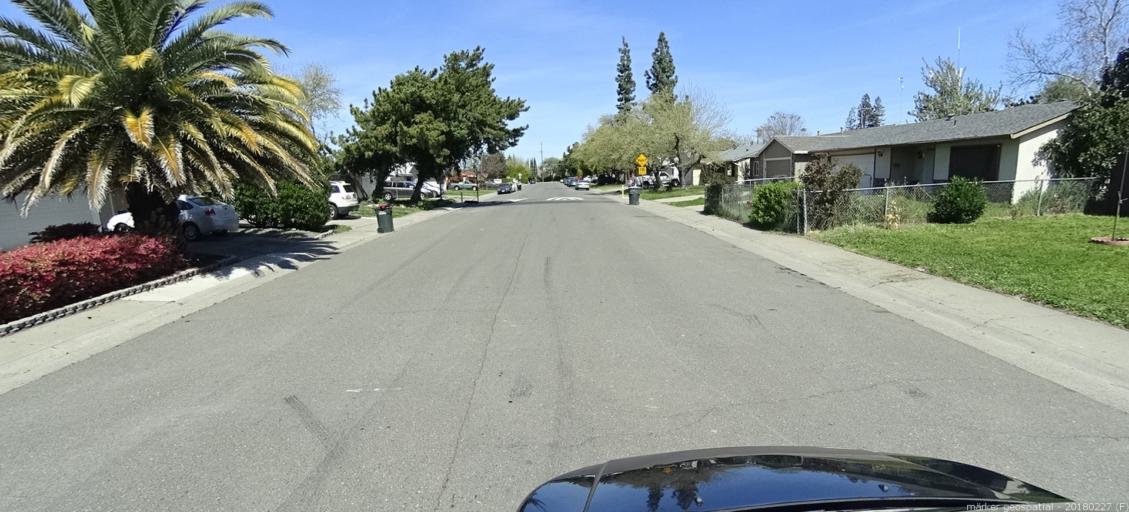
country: US
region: California
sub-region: Sacramento County
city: La Riviera
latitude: 38.5526
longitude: -121.3398
